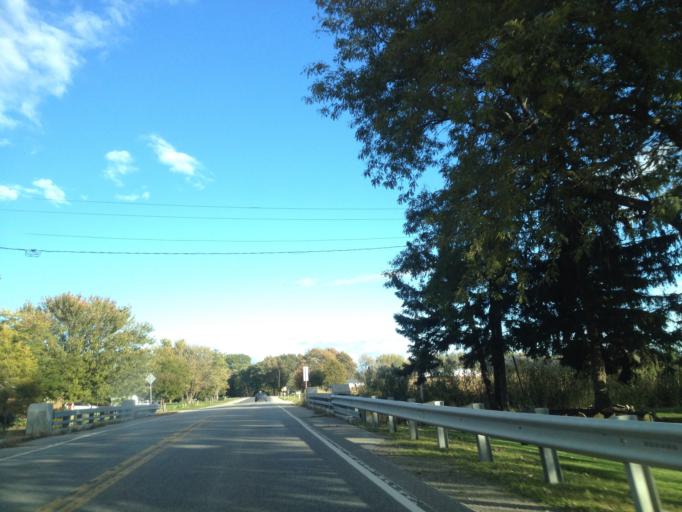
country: US
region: Michigan
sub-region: Wayne County
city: Grosse Pointe Farms
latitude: 42.2972
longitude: -82.6691
